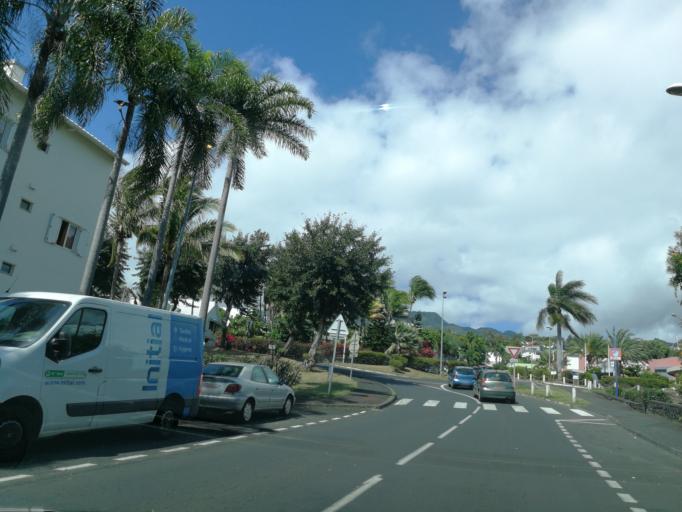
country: RE
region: Reunion
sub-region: Reunion
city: Saint-Denis
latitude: -20.9095
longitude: 55.4823
